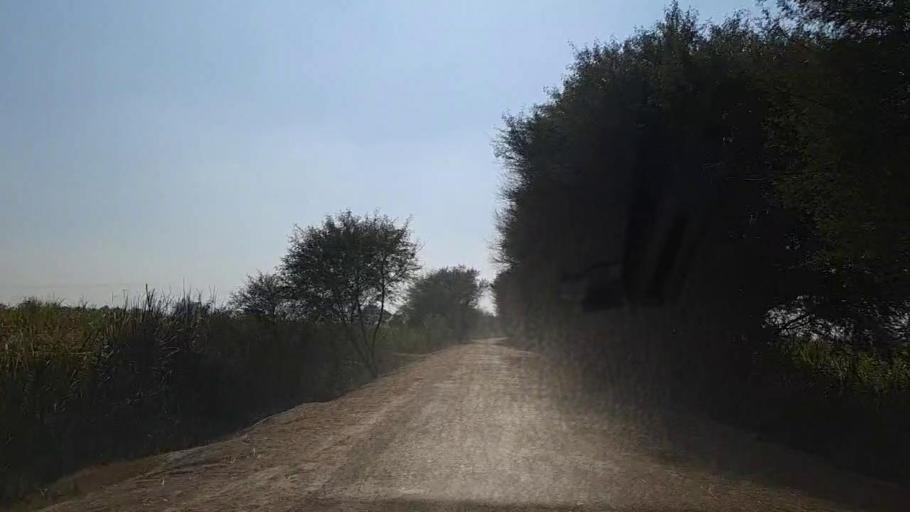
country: PK
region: Sindh
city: Daur
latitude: 26.5062
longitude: 68.3402
